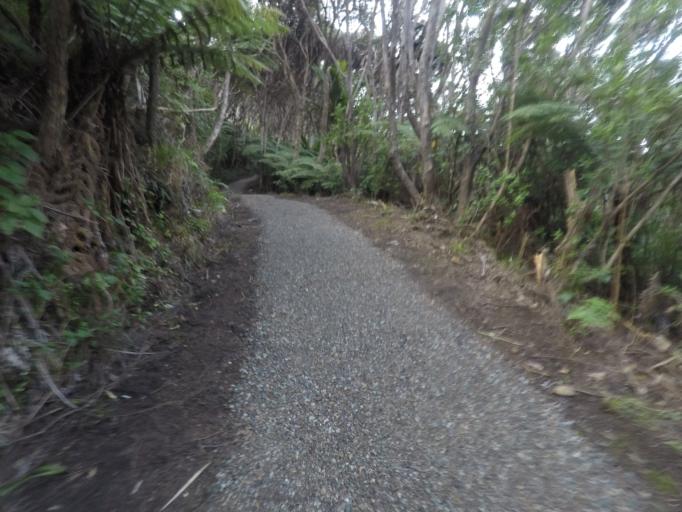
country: NZ
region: Auckland
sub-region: Auckland
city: Muriwai Beach
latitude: -36.9794
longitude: 174.4735
